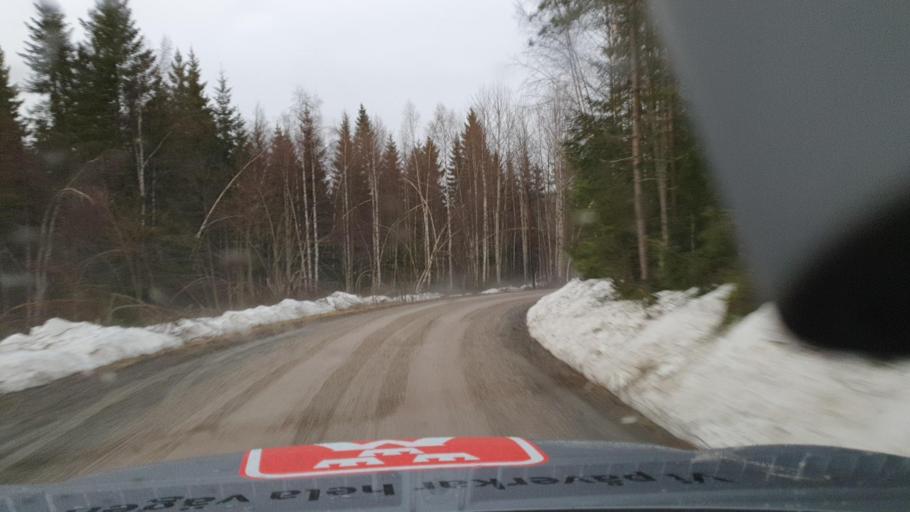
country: SE
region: Vaesternorrland
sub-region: OErnskoeldsviks Kommun
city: Bjasta
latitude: 63.2192
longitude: 18.2906
